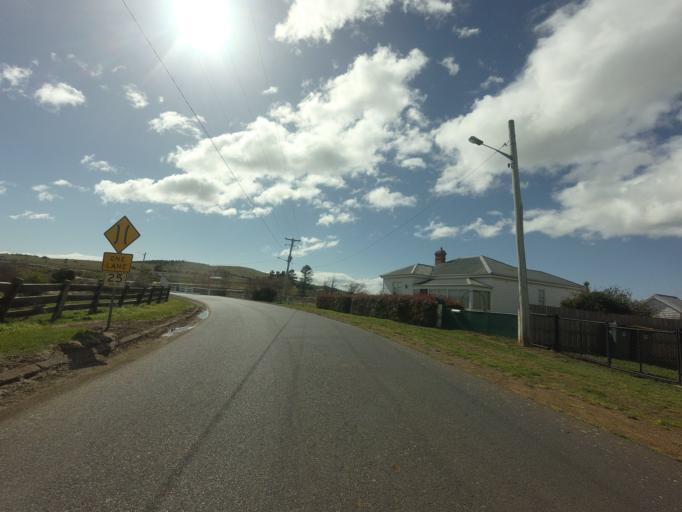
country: AU
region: Tasmania
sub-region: Northern Midlands
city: Evandale
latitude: -42.1326
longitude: 147.4289
